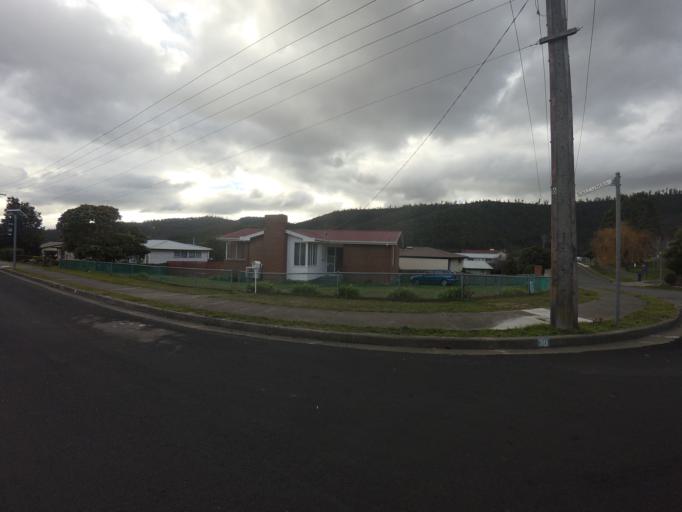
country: AU
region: Tasmania
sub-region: Clarence
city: Warrane
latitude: -42.8581
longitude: 147.3991
